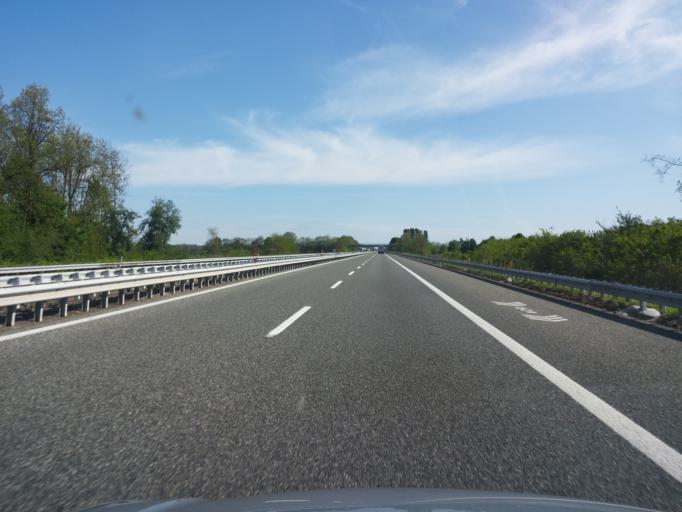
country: IT
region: Piedmont
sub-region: Provincia di Novara
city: Ghemme
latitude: 45.5750
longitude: 8.4092
